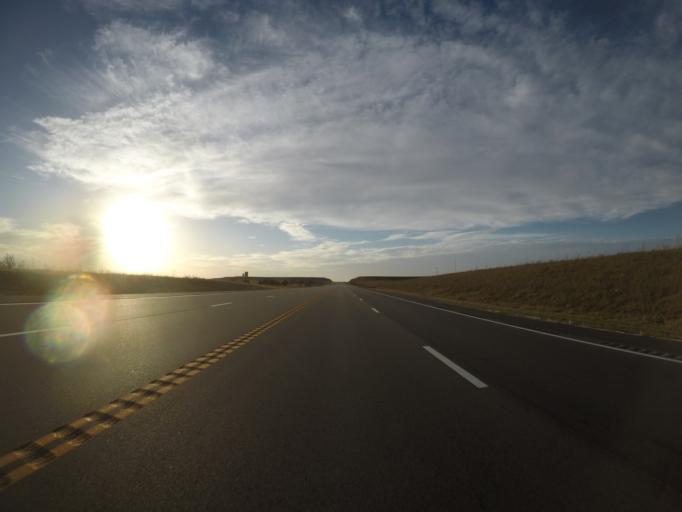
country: US
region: Kansas
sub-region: Chase County
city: Cottonwood Falls
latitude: 38.3990
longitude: -96.5149
